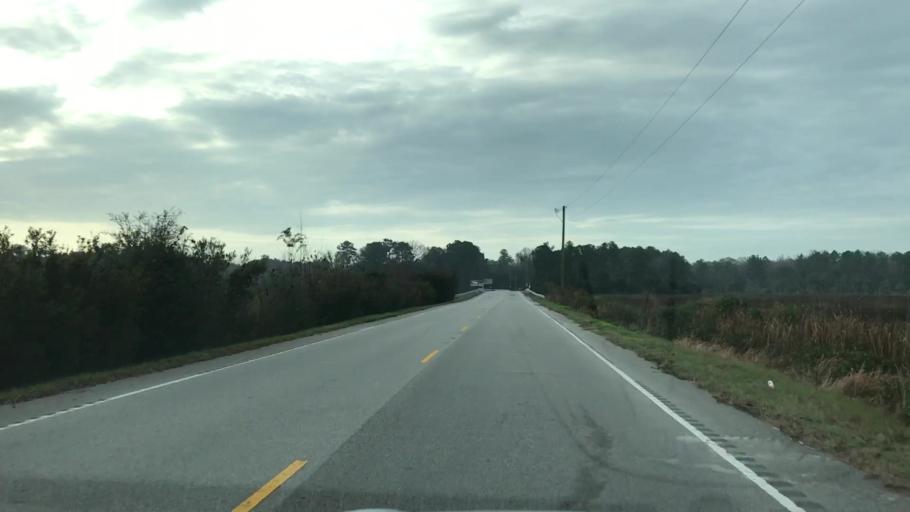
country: US
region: South Carolina
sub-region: Jasper County
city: Ridgeland
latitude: 32.5455
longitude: -80.9126
